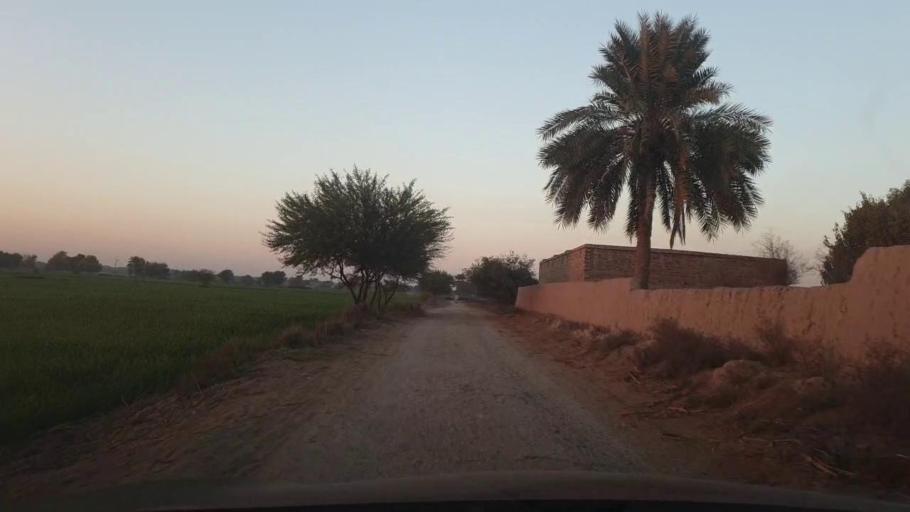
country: PK
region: Sindh
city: Ubauro
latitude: 28.1687
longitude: 69.6356
